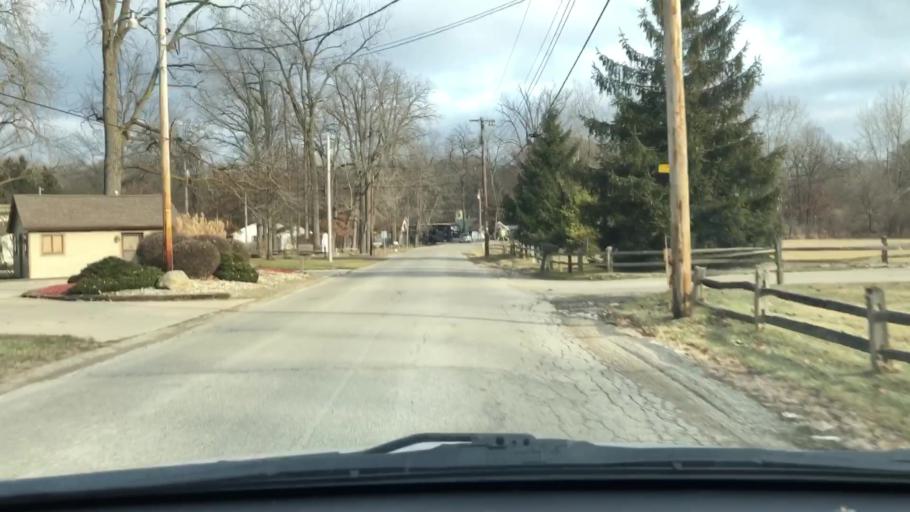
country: US
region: Indiana
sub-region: Steuben County
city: Angola
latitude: 41.6809
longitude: -85.0211
